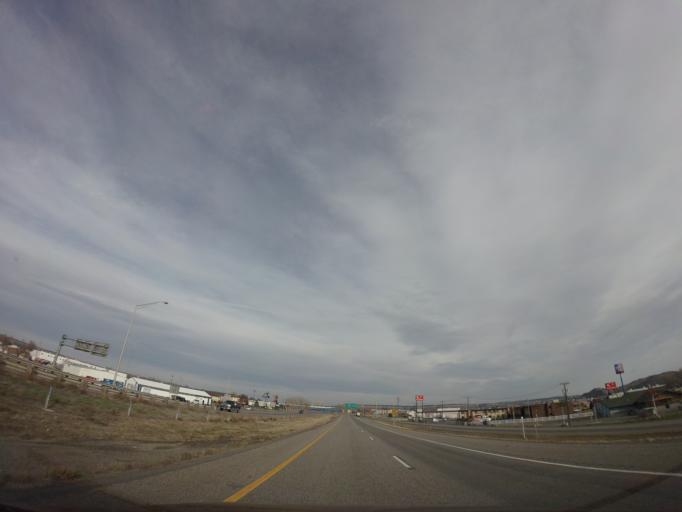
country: US
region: Montana
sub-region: Yellowstone County
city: Billings
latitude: 45.7510
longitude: -108.5524
